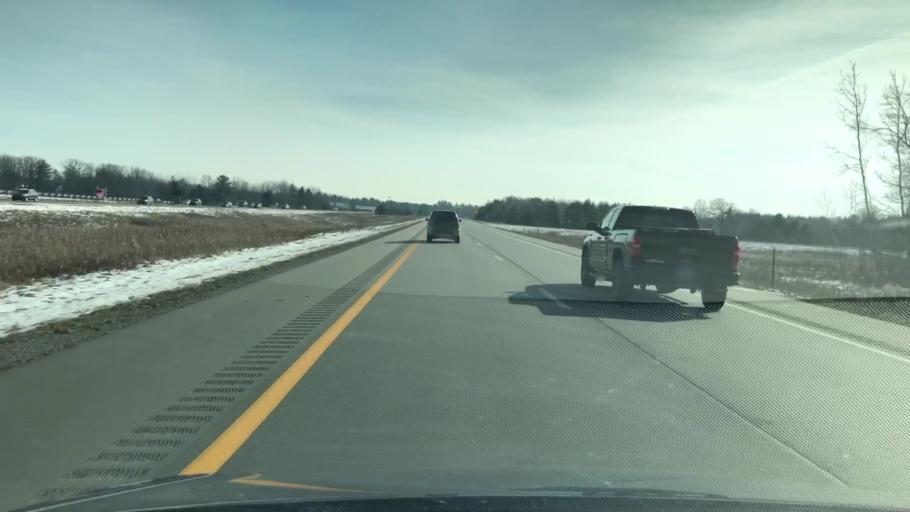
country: US
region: Michigan
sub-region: Ogemaw County
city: Skidway Lake
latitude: 44.1296
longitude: -84.1301
